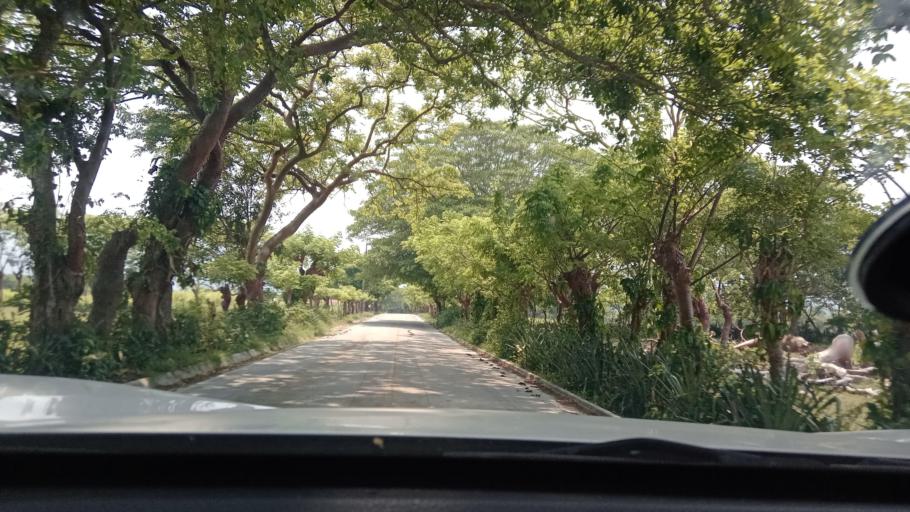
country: MX
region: Veracruz
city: Catemaco
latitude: 18.5607
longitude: -95.0293
